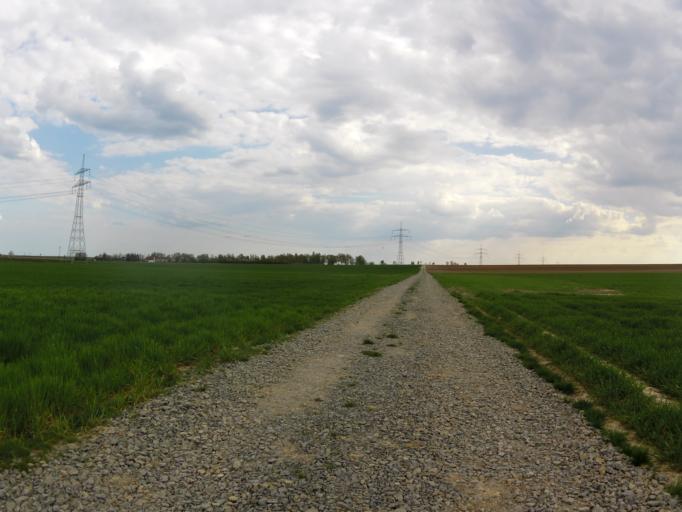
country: DE
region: Bavaria
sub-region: Regierungsbezirk Unterfranken
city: Oberpleichfeld
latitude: 49.8617
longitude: 10.0946
